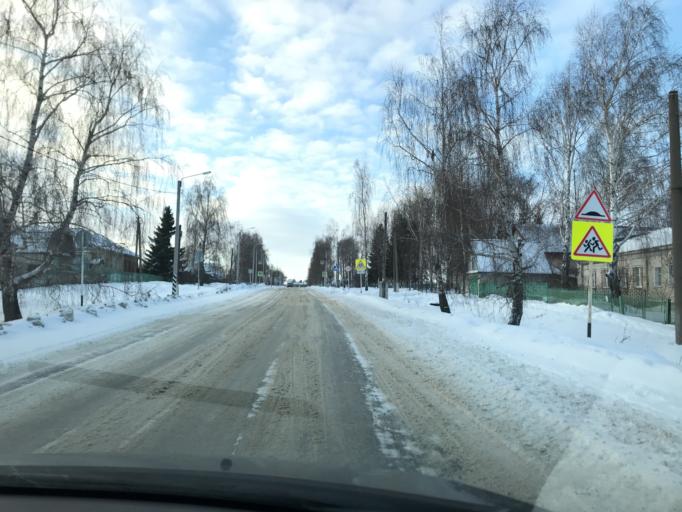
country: RU
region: Ulyanovsk
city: Undory
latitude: 54.6096
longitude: 48.3895
